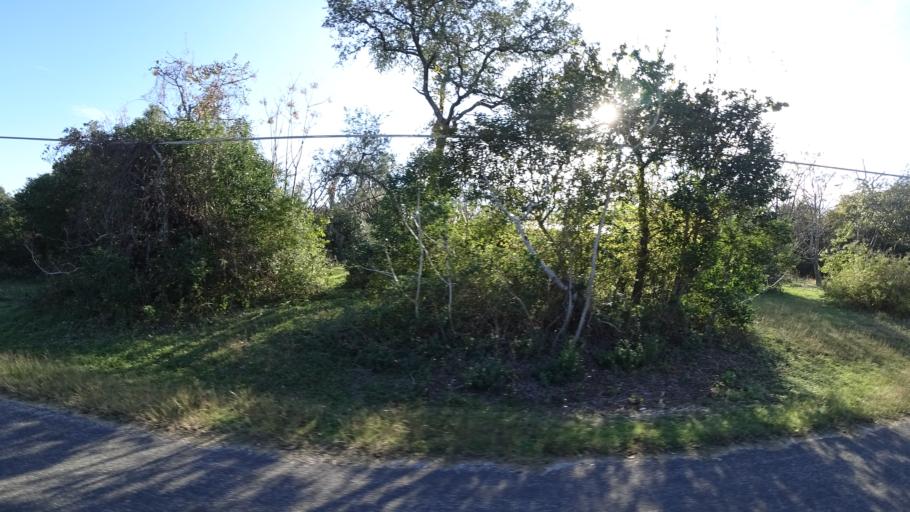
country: US
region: Texas
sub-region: Travis County
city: Barton Creek
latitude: 30.2380
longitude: -97.9126
